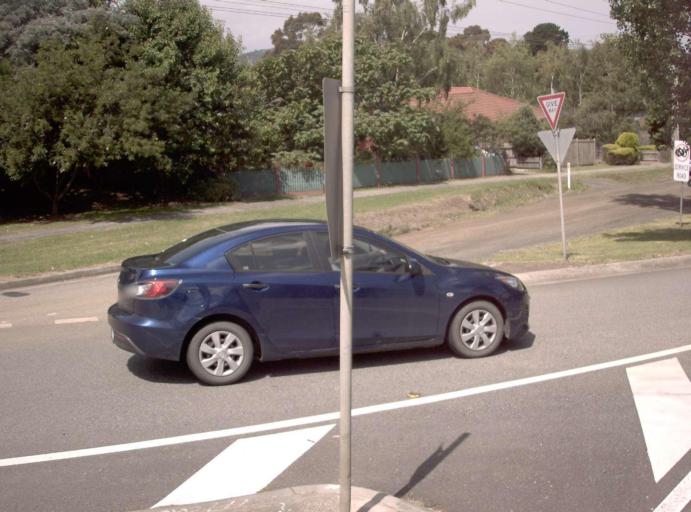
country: AU
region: Victoria
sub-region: Casey
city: Berwick
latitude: -38.0358
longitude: 145.3546
